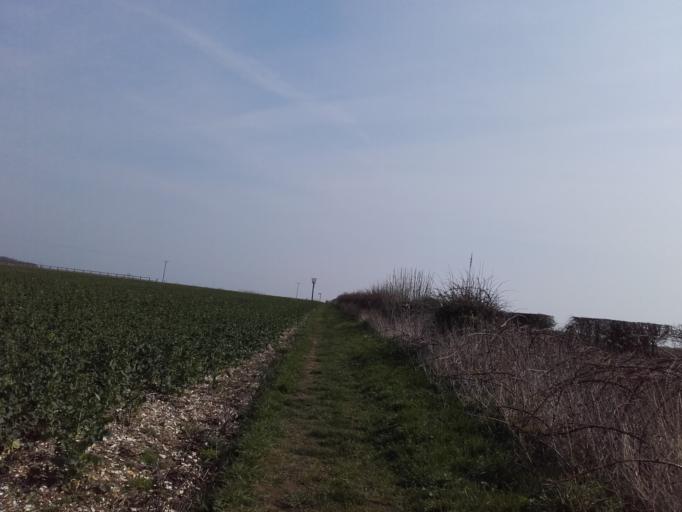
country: GB
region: England
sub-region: East Riding of Yorkshire
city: South Cave
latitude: 53.8028
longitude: -0.5753
